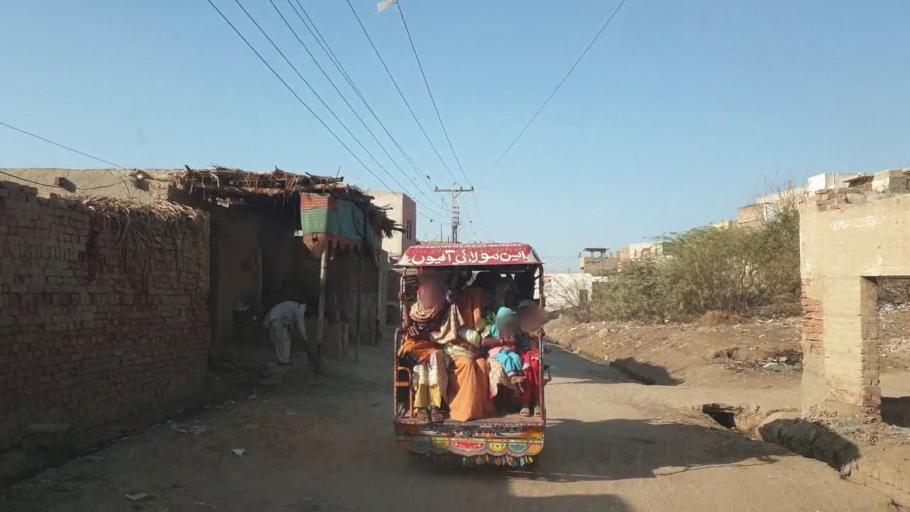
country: PK
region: Sindh
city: Tando Allahyar
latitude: 25.3883
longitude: 68.6759
